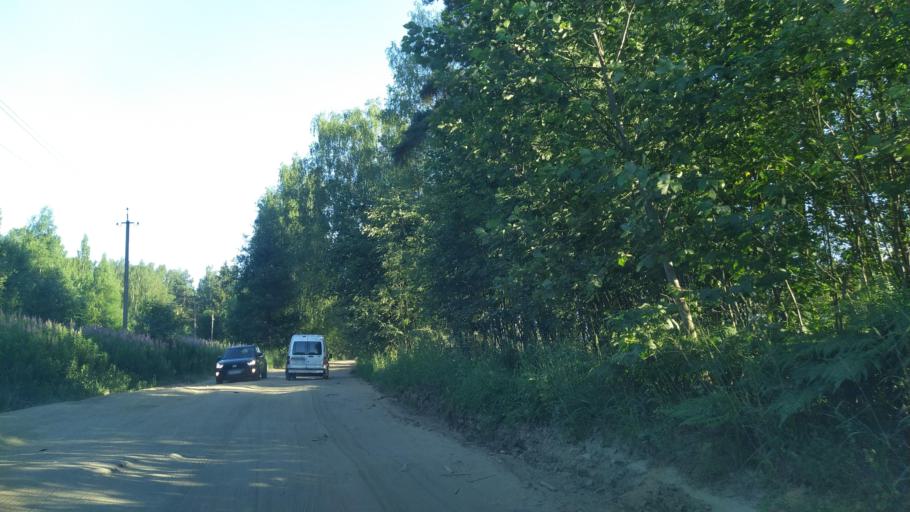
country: RU
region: Leningrad
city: Koltushi
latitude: 59.9092
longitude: 30.7365
